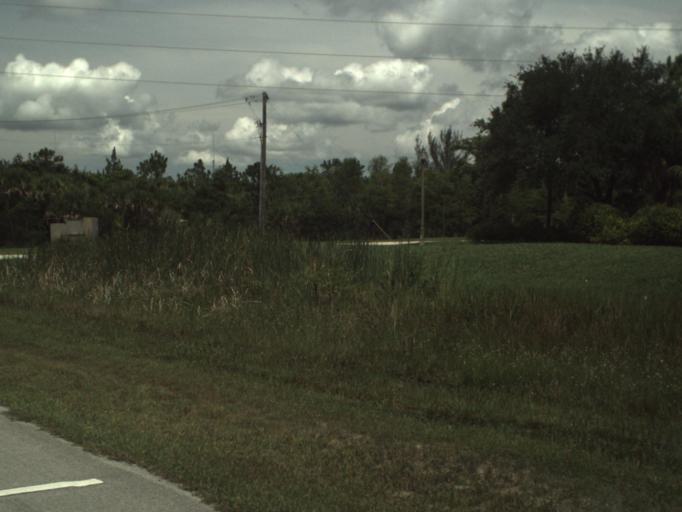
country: US
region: Florida
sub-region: Palm Beach County
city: Palm Beach Gardens
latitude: 26.8400
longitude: -80.1624
